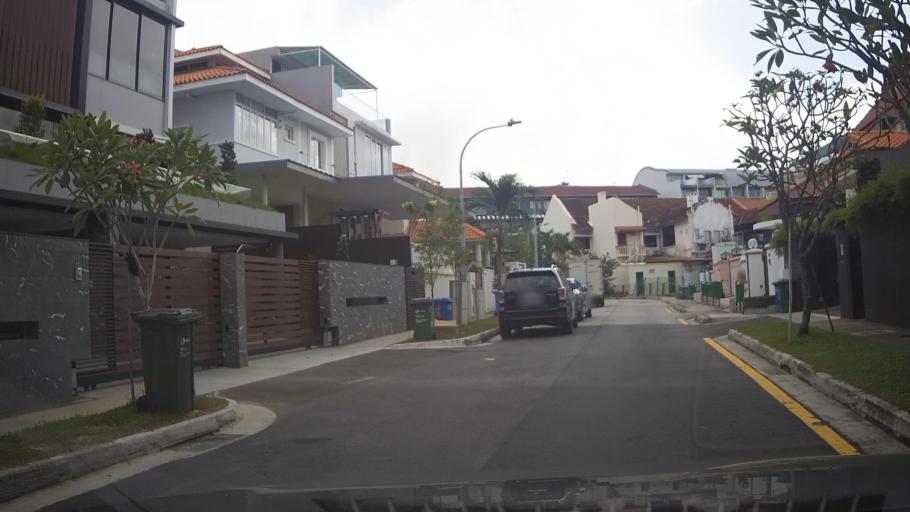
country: SG
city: Singapore
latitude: 1.3079
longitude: 103.8941
